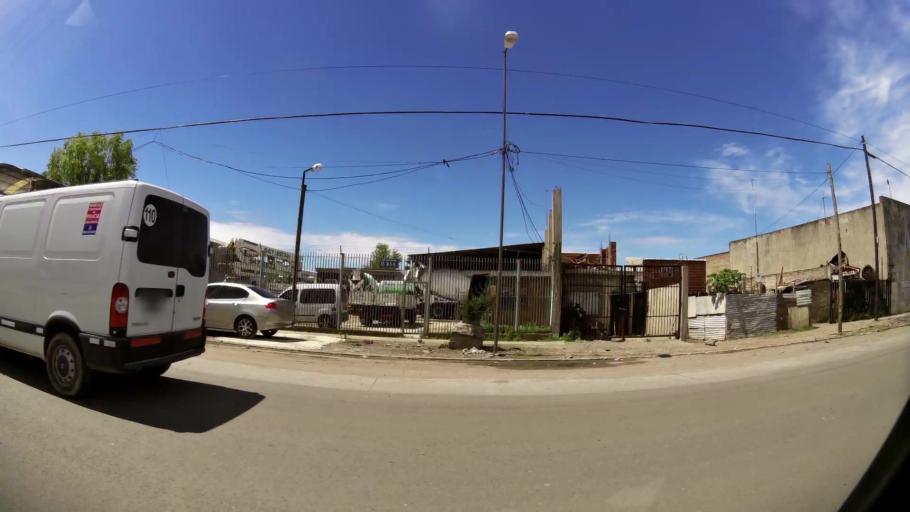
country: AR
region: Buenos Aires
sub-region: Partido de Quilmes
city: Quilmes
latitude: -34.7500
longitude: -58.3064
